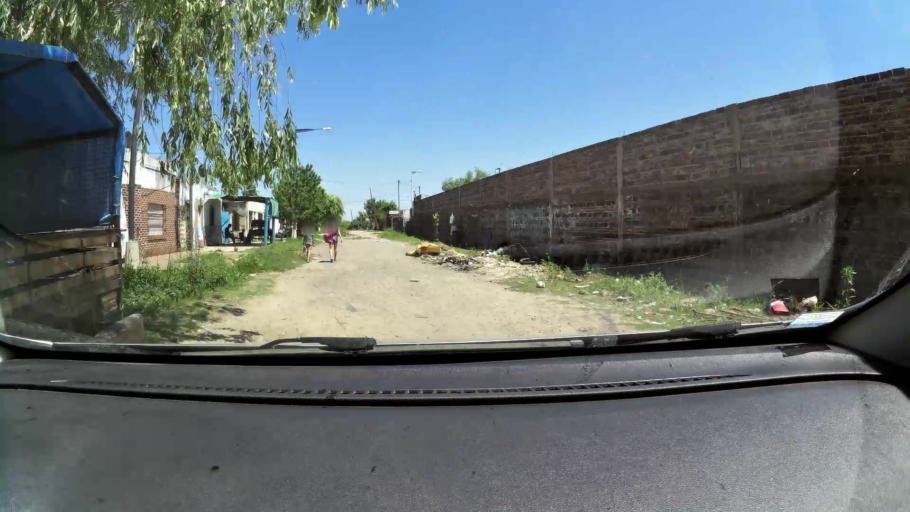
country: AR
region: Santa Fe
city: Santa Fe de la Vera Cruz
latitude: -31.6193
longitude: -60.7204
